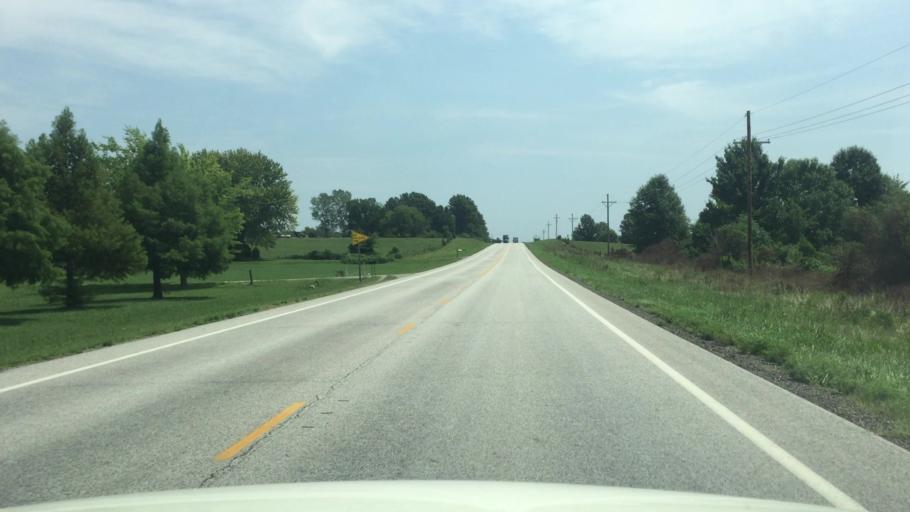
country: US
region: Kansas
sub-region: Cherokee County
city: Columbus
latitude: 37.1780
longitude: -94.7926
